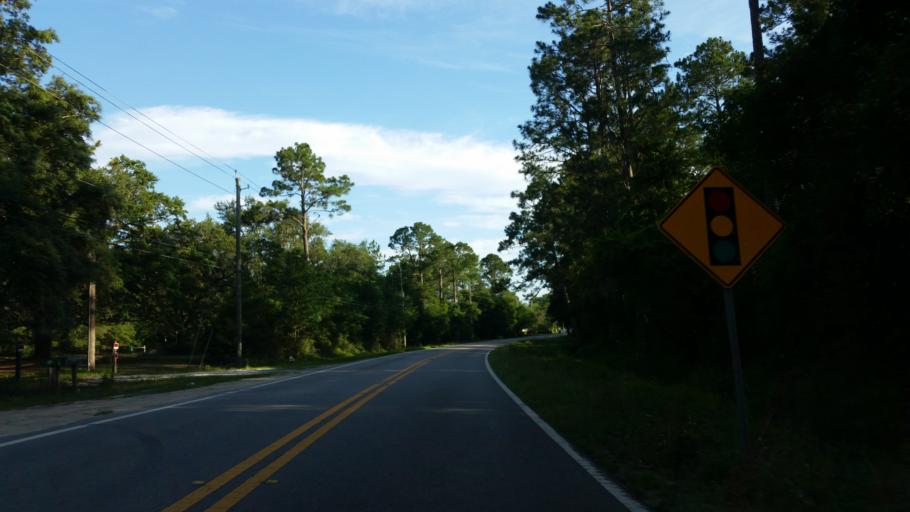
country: US
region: Florida
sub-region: Escambia County
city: Myrtle Grove
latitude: 30.4002
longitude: -87.3735
